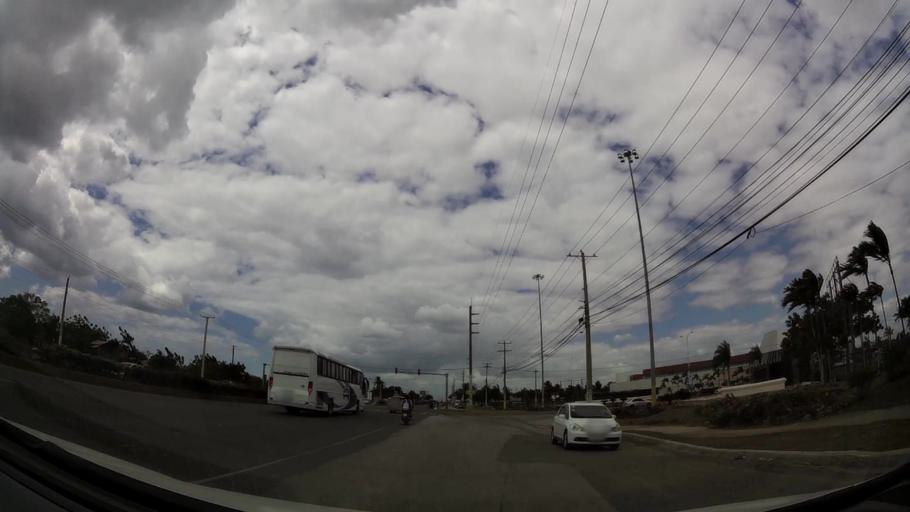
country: DO
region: Santo Domingo
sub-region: Santo Domingo
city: Boca Chica
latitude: 18.4496
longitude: -69.6633
